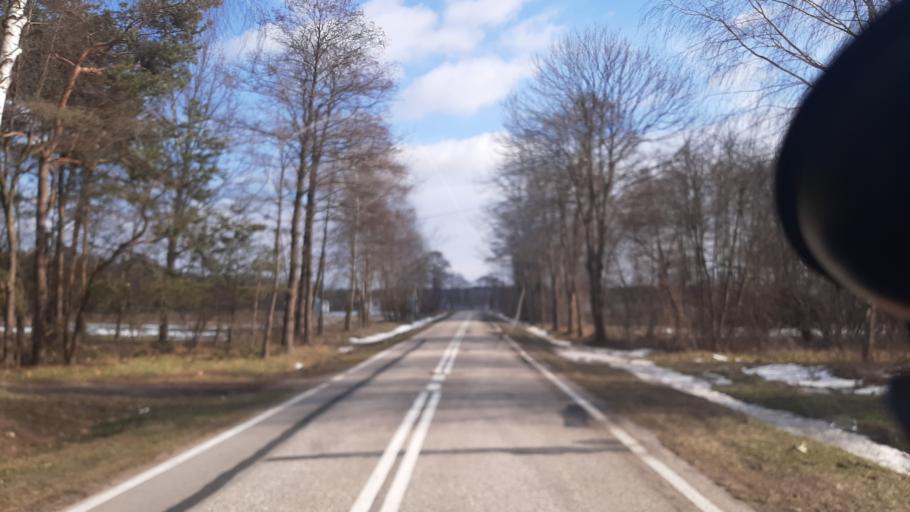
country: PL
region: Lublin Voivodeship
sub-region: Powiat wlodawski
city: Urszulin
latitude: 51.4989
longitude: 23.2543
